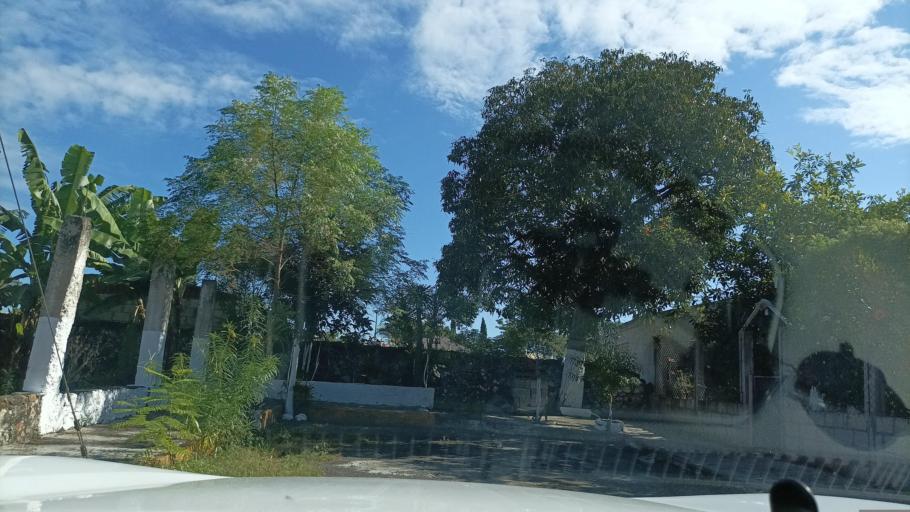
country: MX
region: Veracruz
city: Paso del Macho
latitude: 18.9657
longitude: -96.7182
